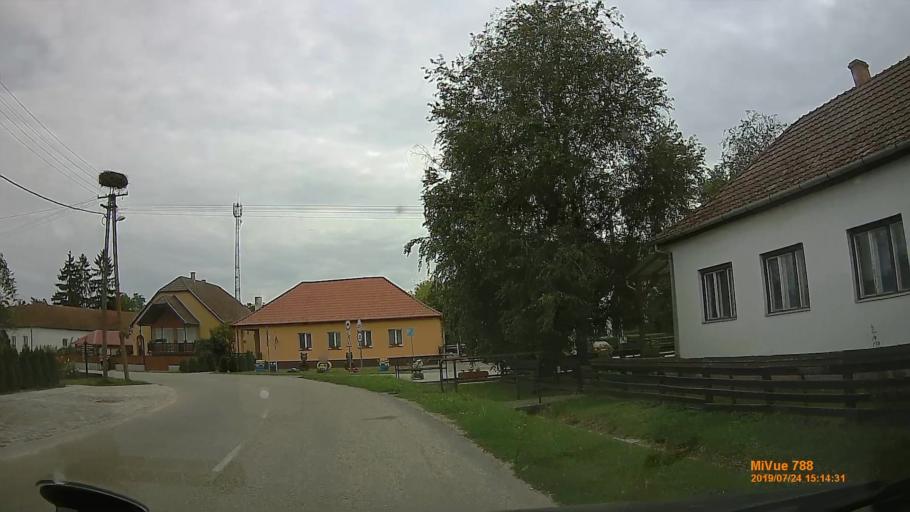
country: HU
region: Szabolcs-Szatmar-Bereg
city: Tarpa
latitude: 48.1993
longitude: 22.5250
